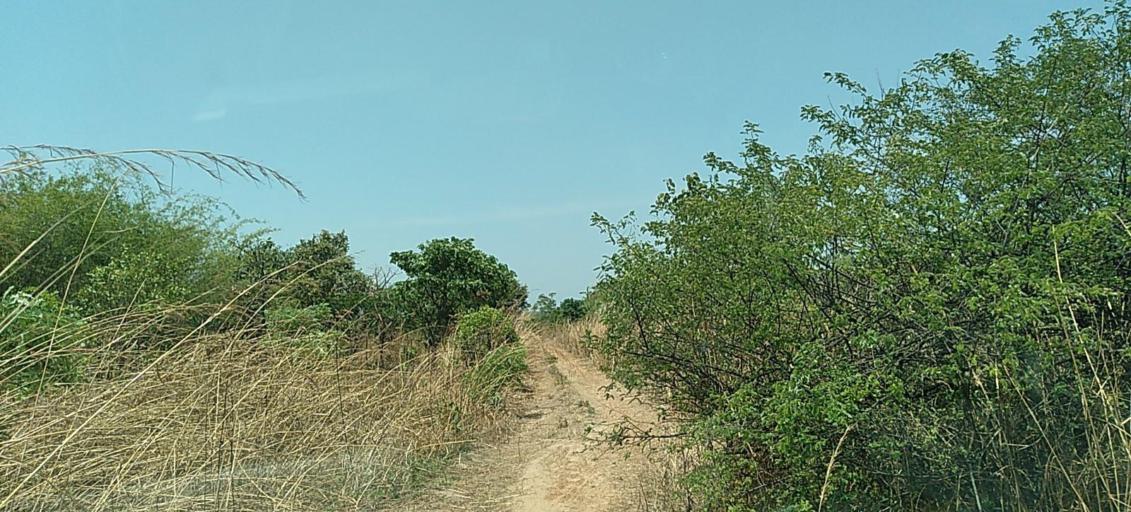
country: ZM
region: Copperbelt
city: Luanshya
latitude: -12.9846
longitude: 28.3277
